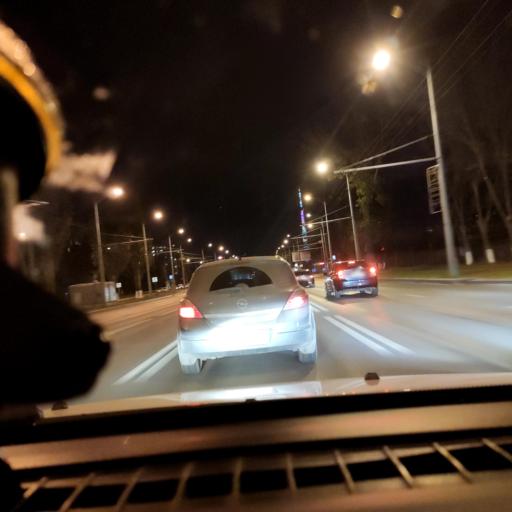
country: RU
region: Samara
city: Samara
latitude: 53.2386
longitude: 50.2043
